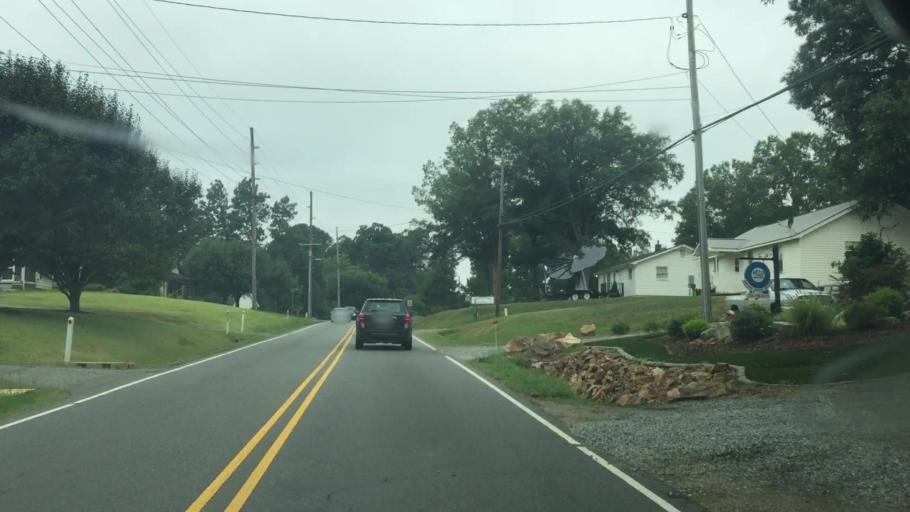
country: US
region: North Carolina
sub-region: Cabarrus County
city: Concord
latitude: 35.4118
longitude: -80.6334
